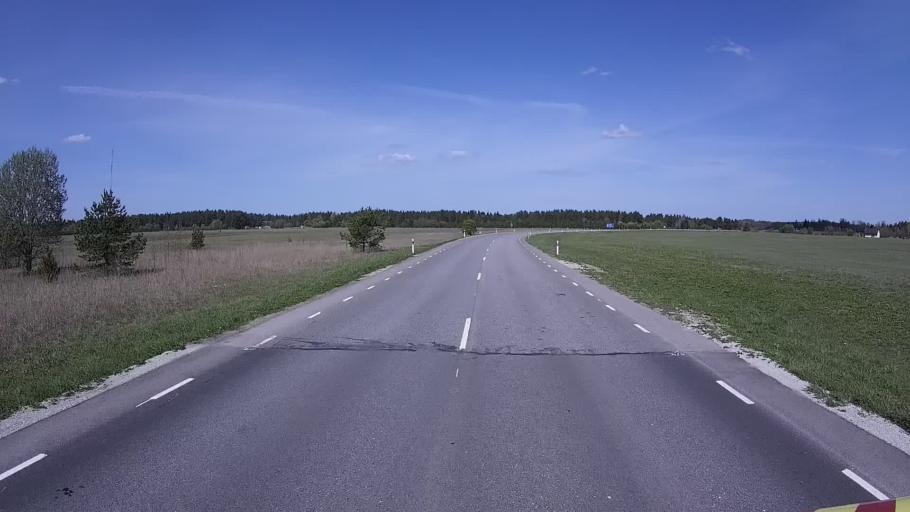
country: EE
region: Harju
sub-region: Paldiski linn
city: Paldiski
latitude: 59.2118
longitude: 24.0944
